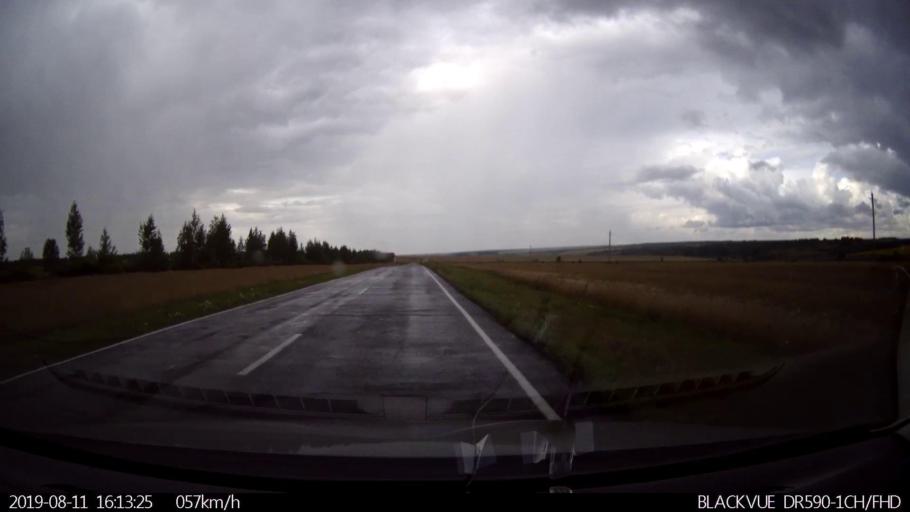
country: RU
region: Ulyanovsk
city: Ignatovka
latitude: 54.0201
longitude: 47.6369
